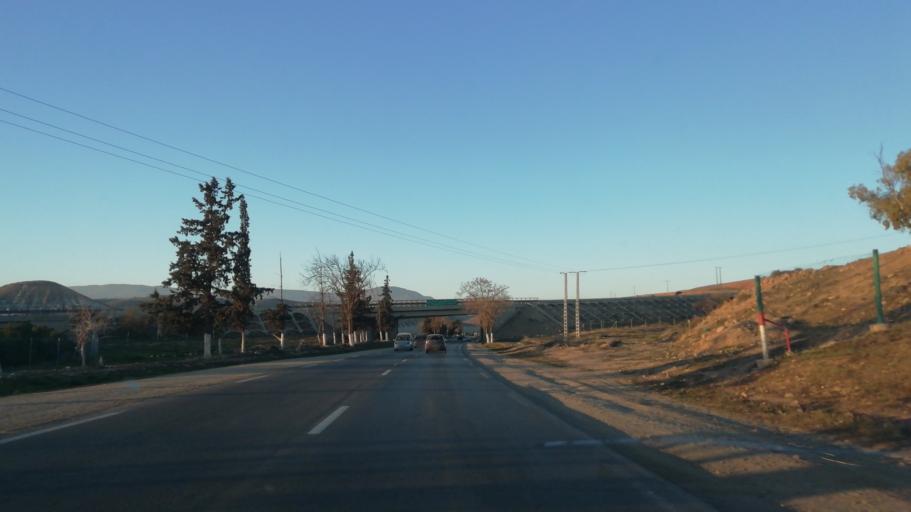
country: DZ
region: Tlemcen
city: Nedroma
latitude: 34.8994
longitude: -1.6390
